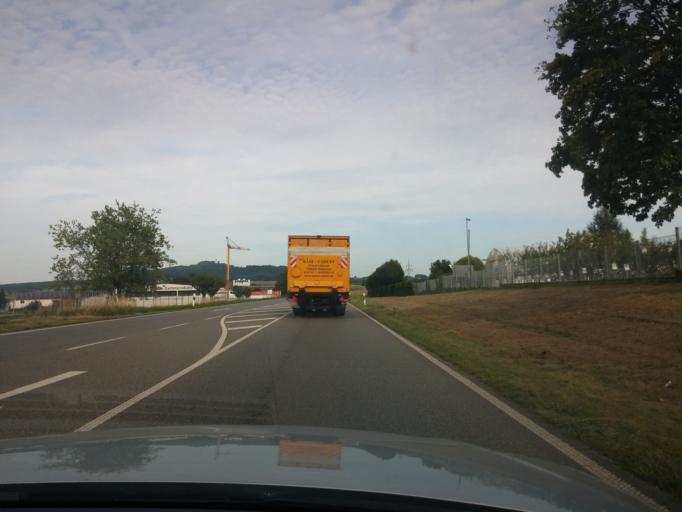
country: DE
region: Baden-Wuerttemberg
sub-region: Tuebingen Region
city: Riedlingen
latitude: 48.1531
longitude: 9.5008
